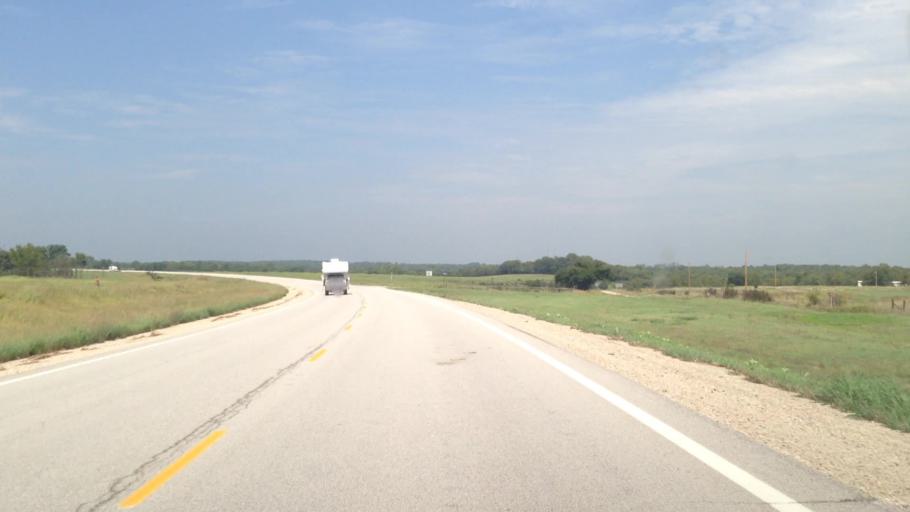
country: US
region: Kansas
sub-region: Anderson County
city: Garnett
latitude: 38.1895
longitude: -95.2412
